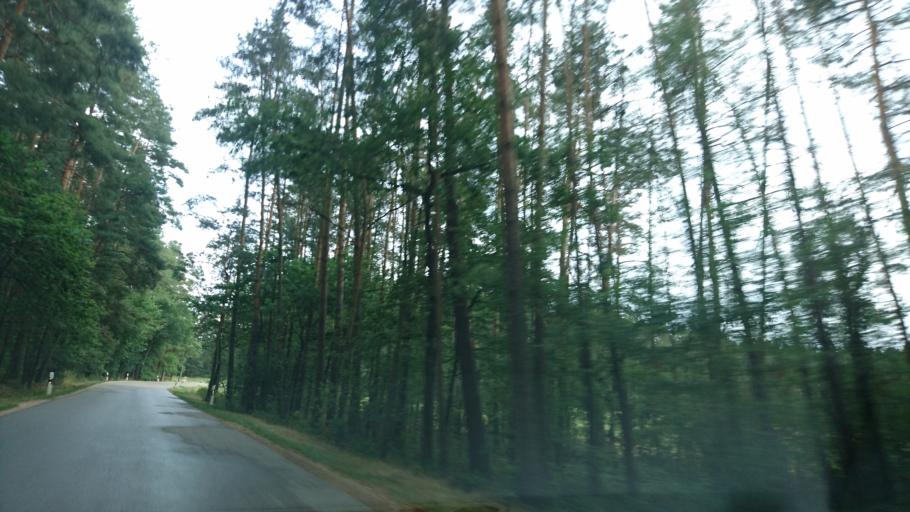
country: DE
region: Bavaria
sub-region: Regierungsbezirk Mittelfranken
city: Roth
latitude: 49.2000
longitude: 11.0929
